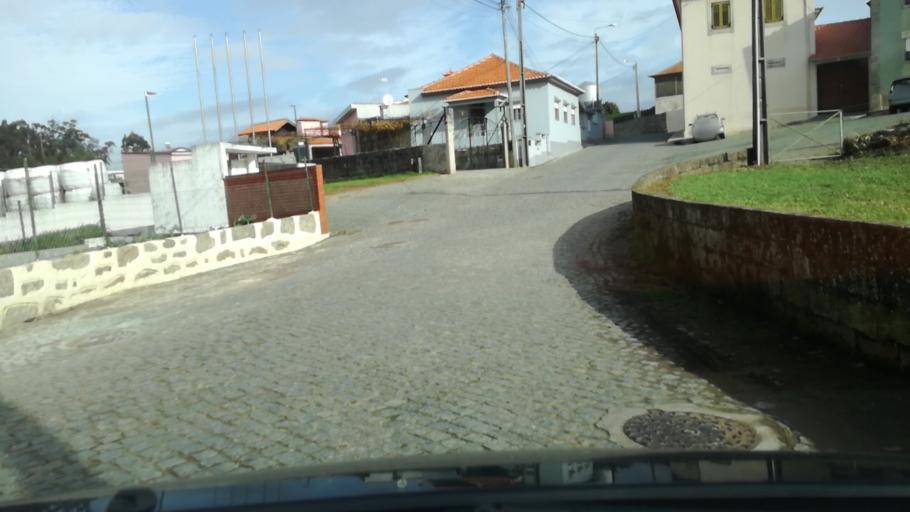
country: PT
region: Porto
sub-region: Maia
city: Gemunde
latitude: 41.2584
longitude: -8.6754
